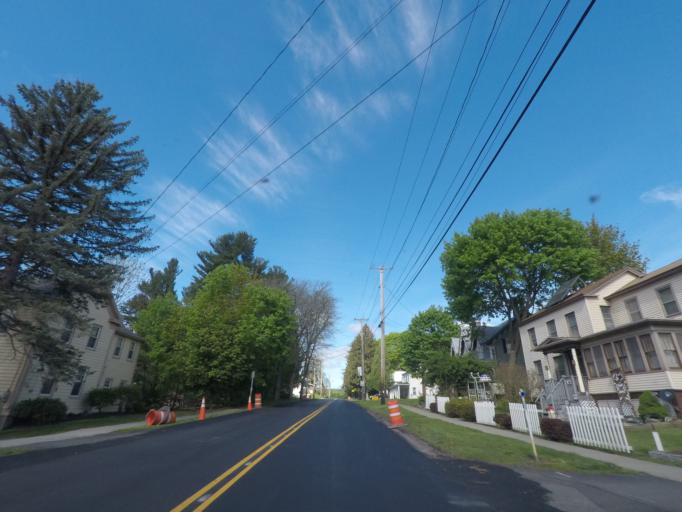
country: US
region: New York
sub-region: Albany County
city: Ravena
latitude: 42.4743
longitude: -73.7957
